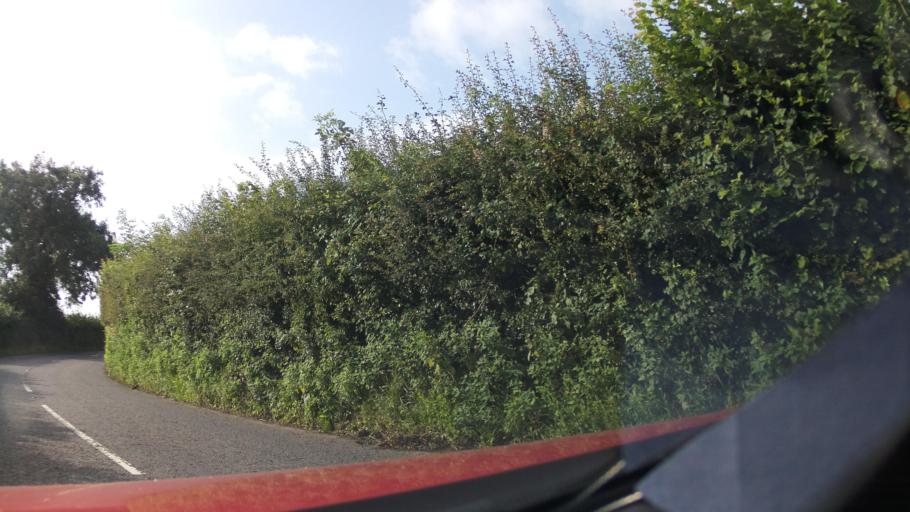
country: GB
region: England
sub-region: North Somerset
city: Winford
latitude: 51.3928
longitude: -2.6645
